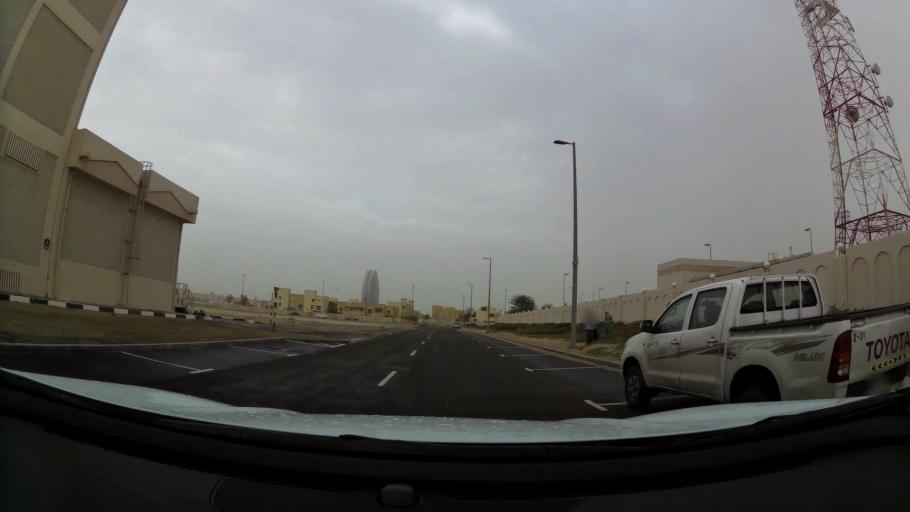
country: AE
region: Abu Dhabi
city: Abu Dhabi
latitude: 24.4329
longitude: 54.5802
